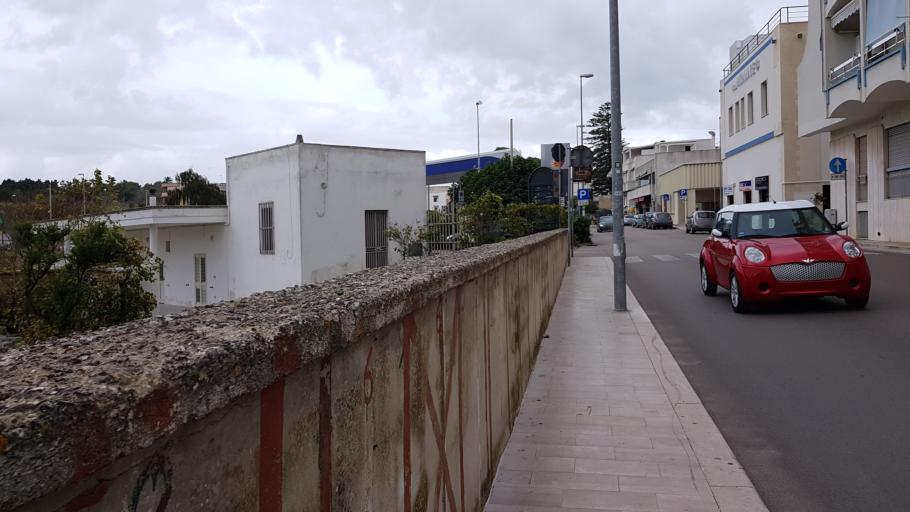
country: IT
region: Apulia
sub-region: Provincia di Lecce
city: Otranto
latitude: 40.1467
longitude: 18.4872
